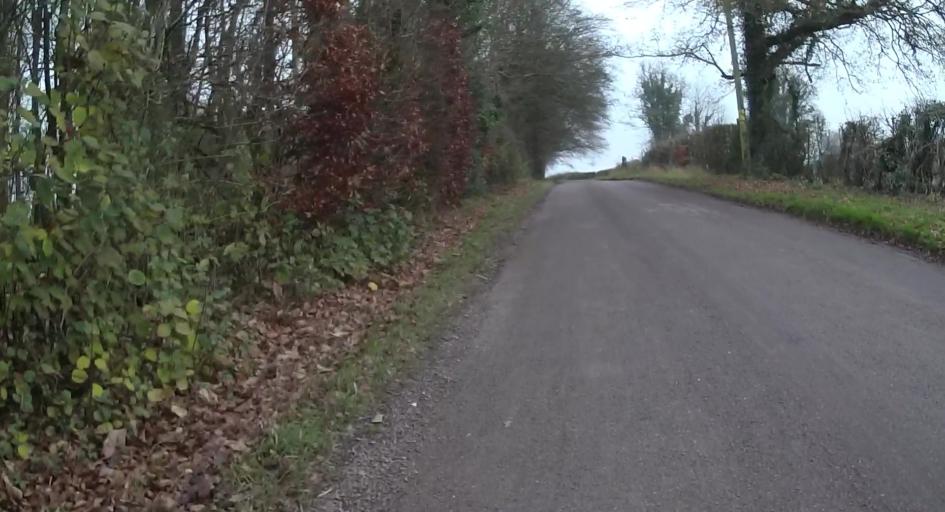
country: GB
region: England
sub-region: Hampshire
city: Kings Worthy
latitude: 51.1263
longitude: -1.2115
